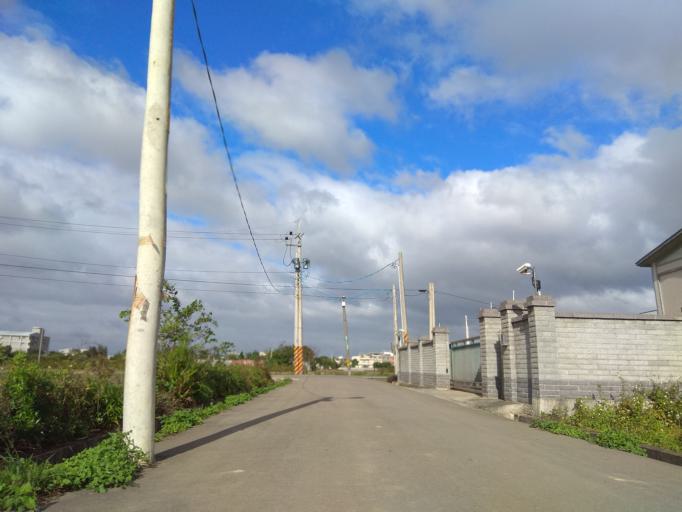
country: TW
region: Taiwan
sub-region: Hsinchu
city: Zhubei
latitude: 24.9705
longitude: 121.0933
